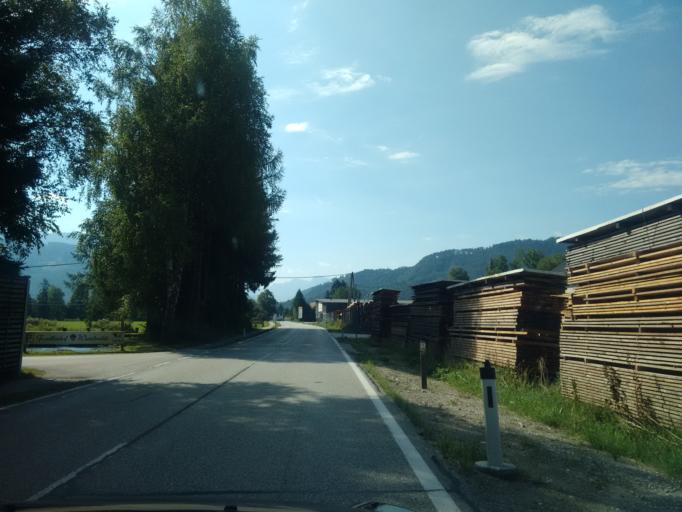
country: AT
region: Upper Austria
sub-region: Politischer Bezirk Gmunden
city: Gruenau im Almtal
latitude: 47.8701
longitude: 13.9442
